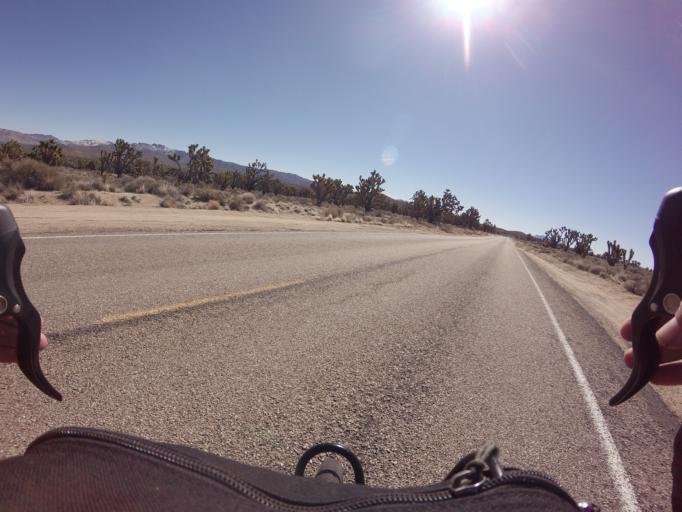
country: US
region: Nevada
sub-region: Clark County
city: Sandy Valley
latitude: 35.2449
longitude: -115.4987
